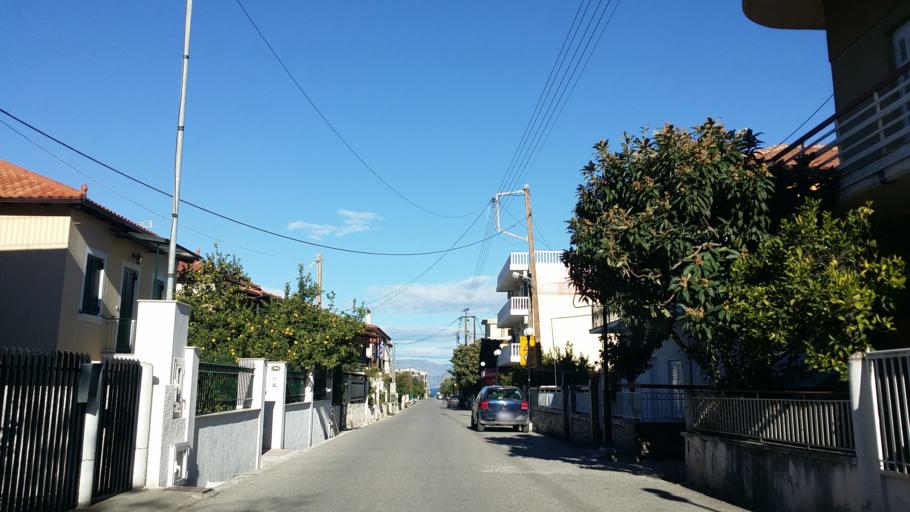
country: GR
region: West Greece
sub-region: Nomos Achaias
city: Temeni
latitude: 38.1933
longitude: 22.1988
